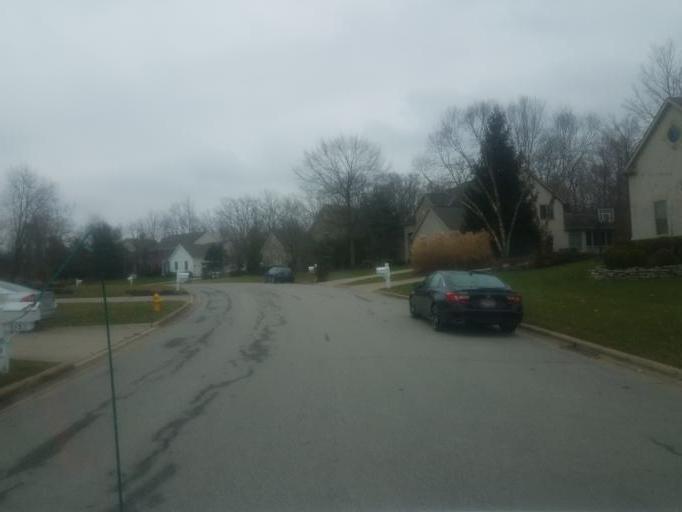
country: US
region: Ohio
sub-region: Franklin County
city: Westerville
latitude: 40.1723
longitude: -82.9420
